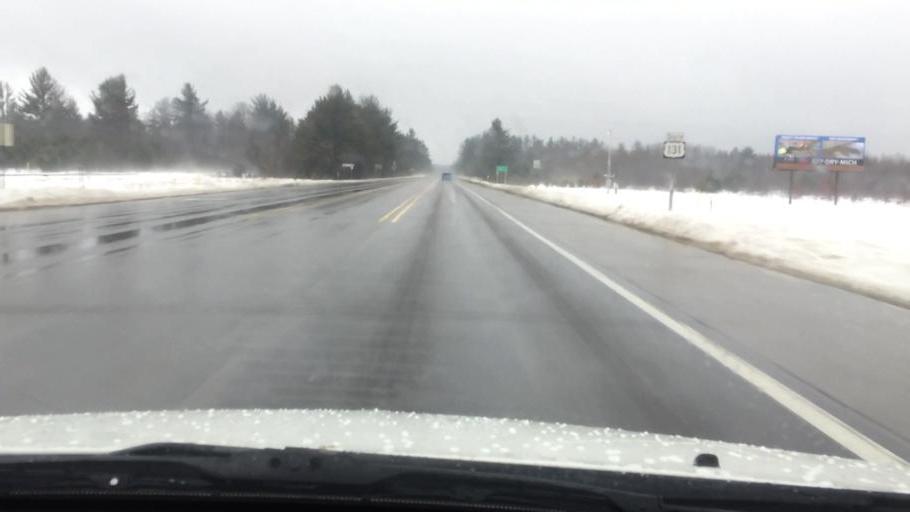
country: US
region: Michigan
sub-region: Kalkaska County
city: Kalkaska
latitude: 44.7167
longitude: -85.1900
